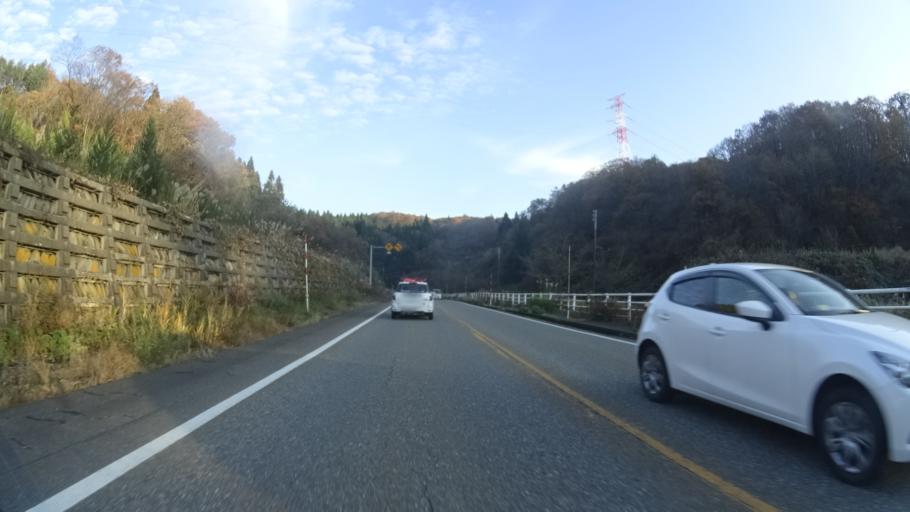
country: JP
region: Niigata
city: Kashiwazaki
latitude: 37.4056
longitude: 138.6889
